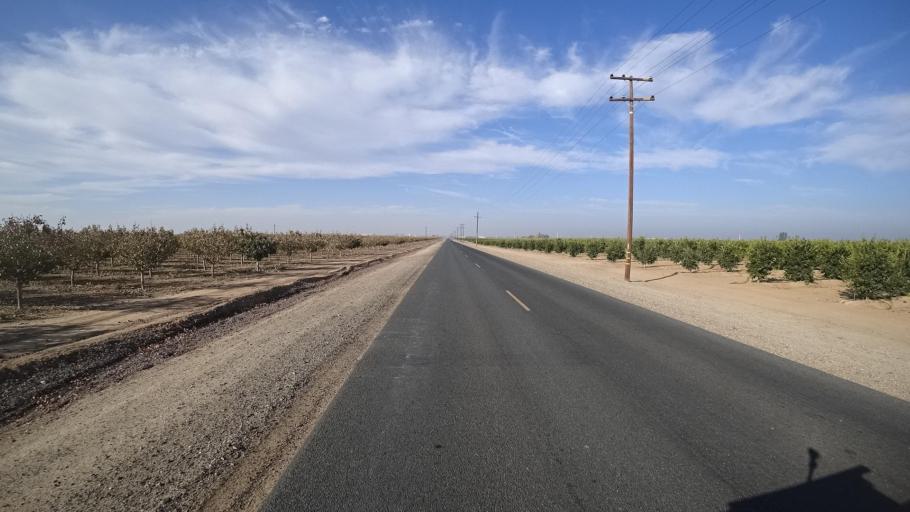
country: US
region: California
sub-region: Kern County
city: McFarland
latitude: 35.6020
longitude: -119.1752
